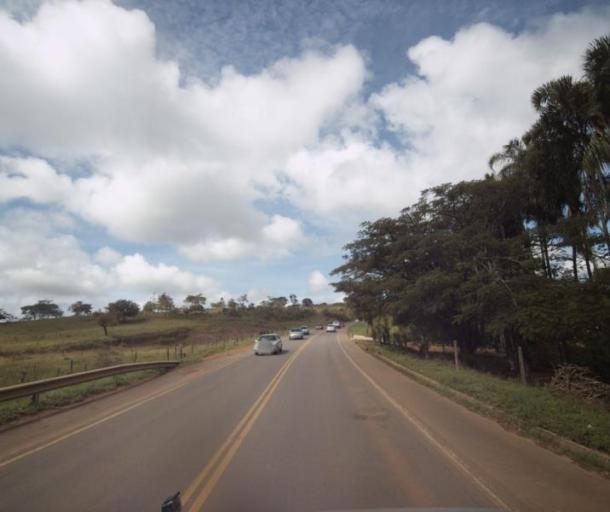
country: BR
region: Goias
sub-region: Pirenopolis
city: Pirenopolis
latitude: -15.9495
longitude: -48.8037
